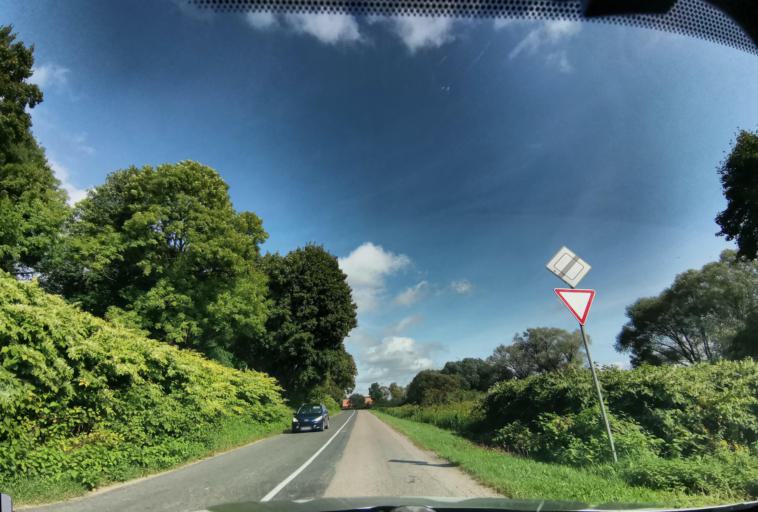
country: RU
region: Kaliningrad
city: Chernyakhovsk
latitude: 54.6583
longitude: 21.8041
